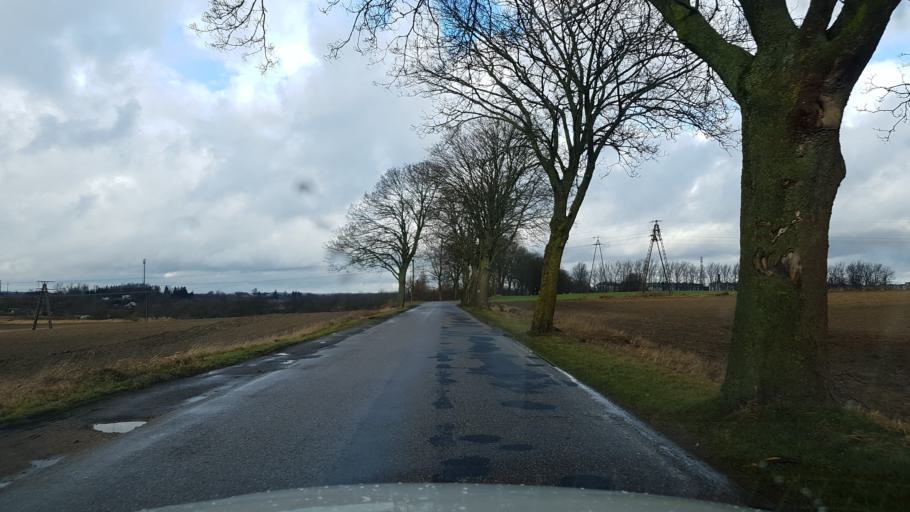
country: PL
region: West Pomeranian Voivodeship
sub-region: Powiat drawski
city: Czaplinek
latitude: 53.5412
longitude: 16.2321
